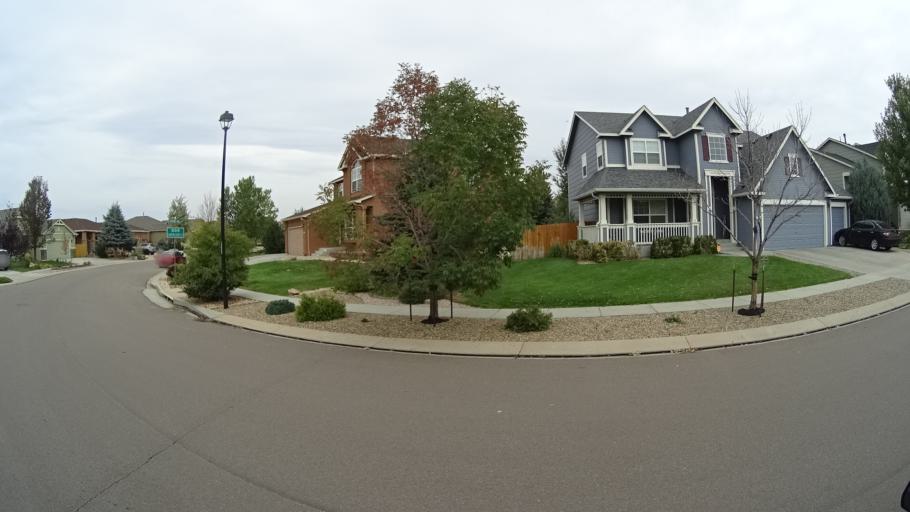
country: US
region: Colorado
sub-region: El Paso County
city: Cimarron Hills
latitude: 38.9185
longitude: -104.6911
